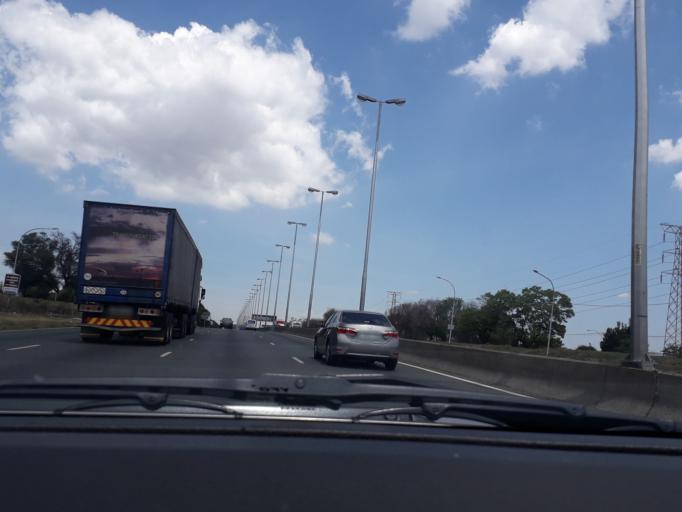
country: ZA
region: Gauteng
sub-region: City of Johannesburg Metropolitan Municipality
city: Johannesburg
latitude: -26.2452
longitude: 28.0055
